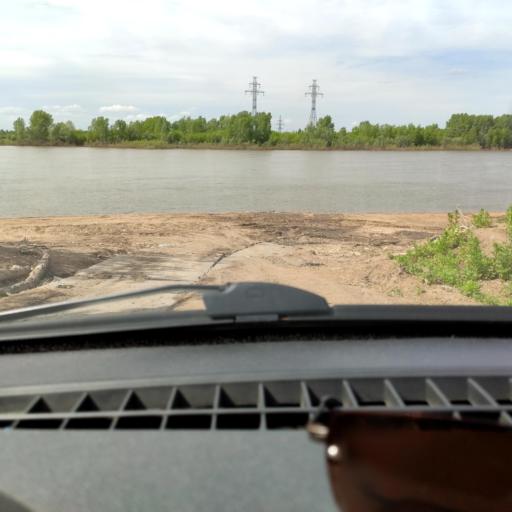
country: RU
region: Bashkortostan
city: Ufa
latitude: 54.8328
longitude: 56.0587
